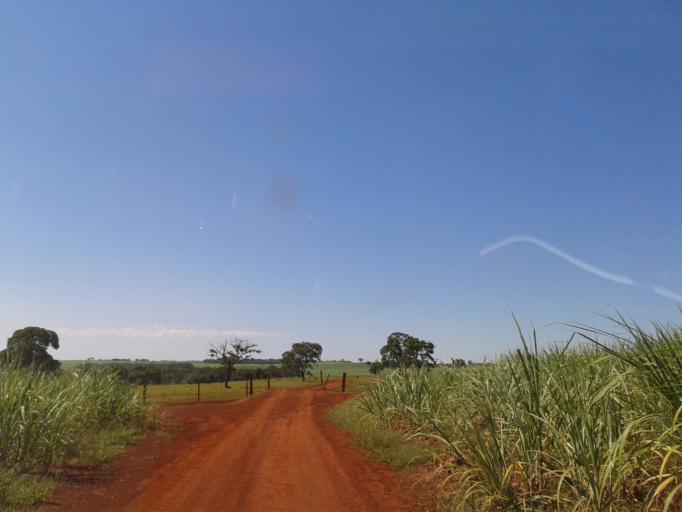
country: BR
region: Minas Gerais
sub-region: Centralina
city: Centralina
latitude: -18.6236
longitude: -49.2583
